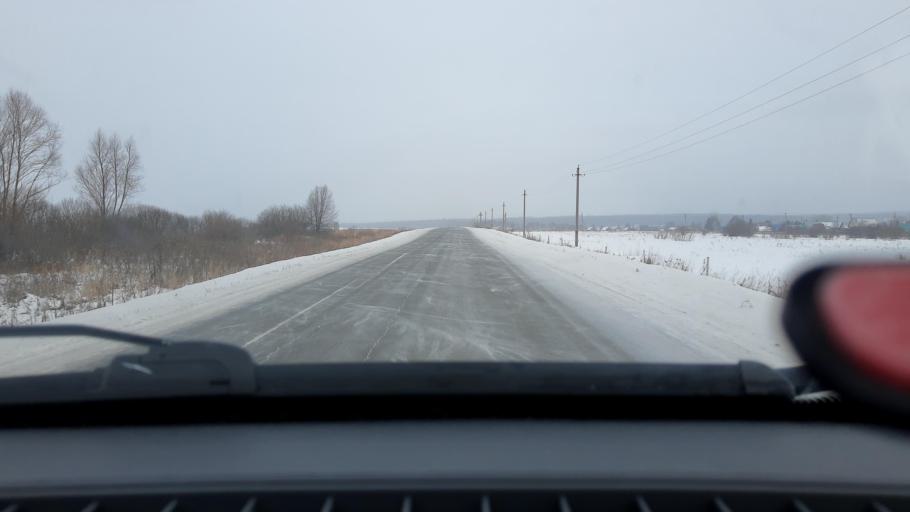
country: RU
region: Bashkortostan
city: Iglino
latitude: 54.7448
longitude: 56.3982
